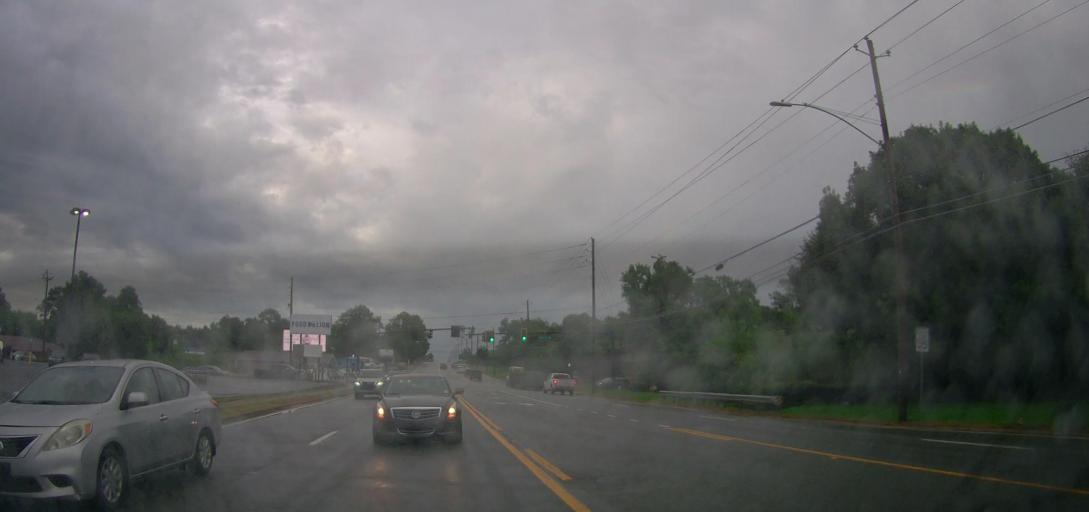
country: US
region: Georgia
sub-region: Ware County
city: Waycross
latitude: 31.2171
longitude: -82.3495
